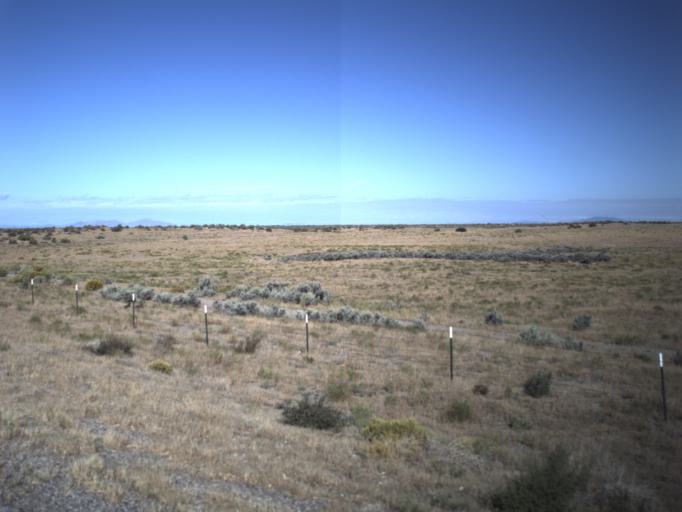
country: US
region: Utah
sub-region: Millard County
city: Delta
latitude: 39.3545
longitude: -112.4089
